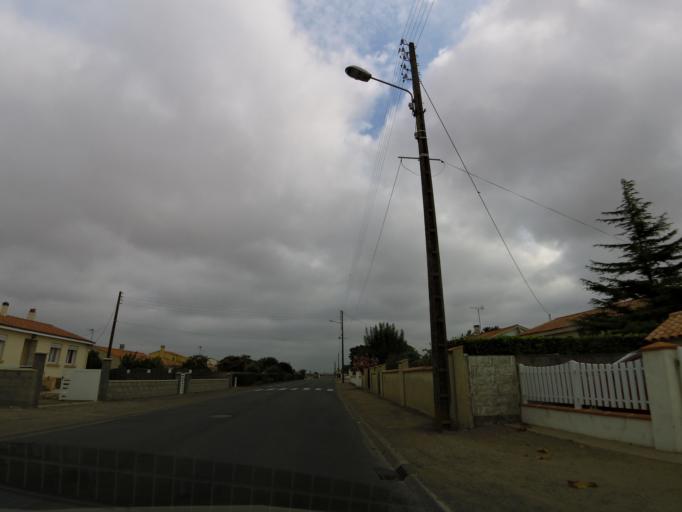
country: FR
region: Pays de la Loire
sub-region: Departement de la Vendee
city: Longeville-sur-Mer
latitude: 46.4268
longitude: -1.4894
